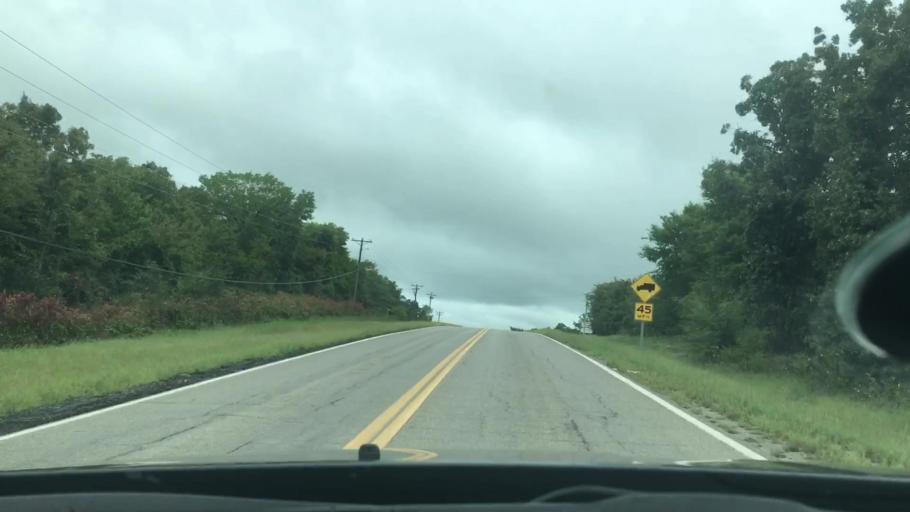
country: US
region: Oklahoma
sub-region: Cherokee County
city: Park Hill
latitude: 35.6893
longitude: -94.9110
